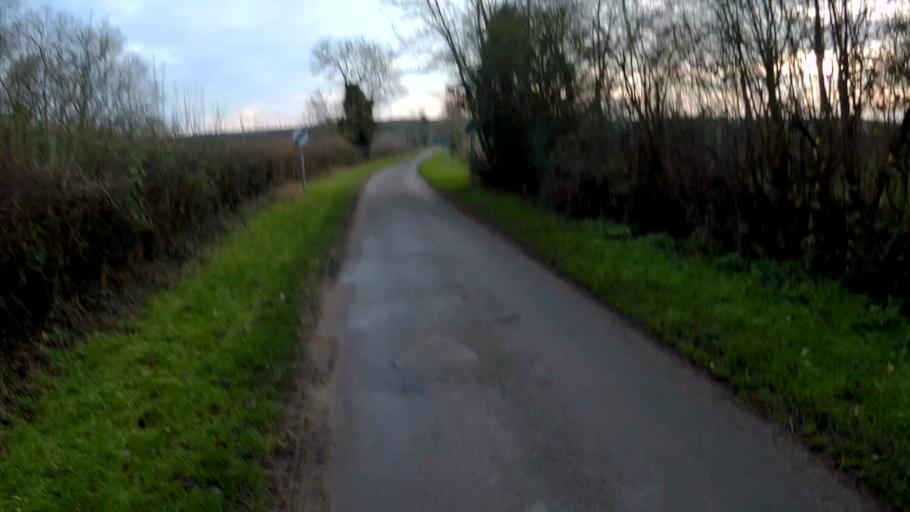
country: GB
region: England
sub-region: Lincolnshire
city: Bourne
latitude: 52.8299
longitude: -0.4058
